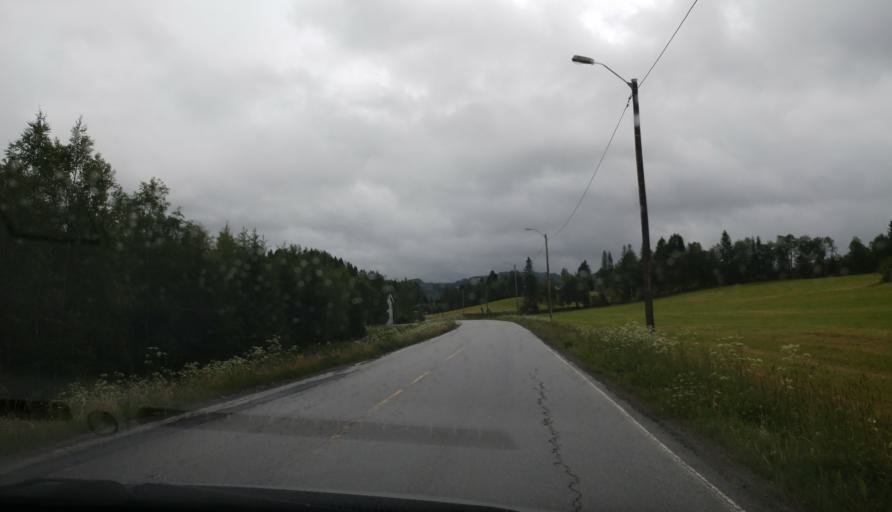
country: NO
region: Sor-Trondelag
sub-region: Selbu
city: Mebonden
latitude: 63.2623
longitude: 11.0814
